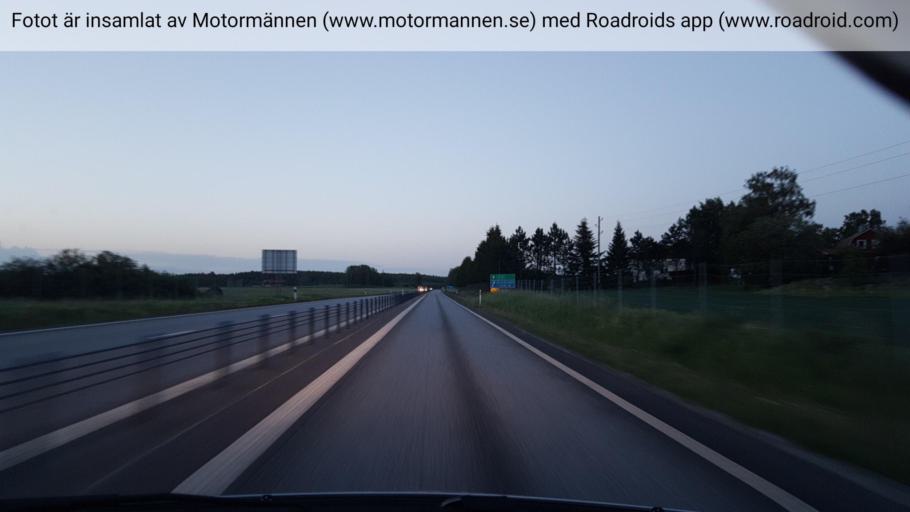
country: SE
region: Vaestmanland
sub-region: Kopings Kommun
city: Koping
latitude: 59.5671
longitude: 16.0785
